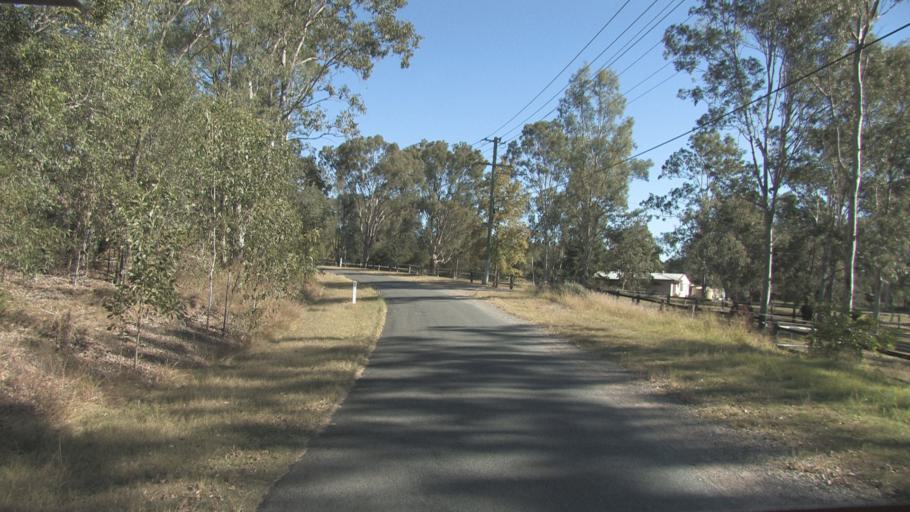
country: AU
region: Queensland
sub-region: Logan
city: North Maclean
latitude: -27.7641
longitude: 153.0253
